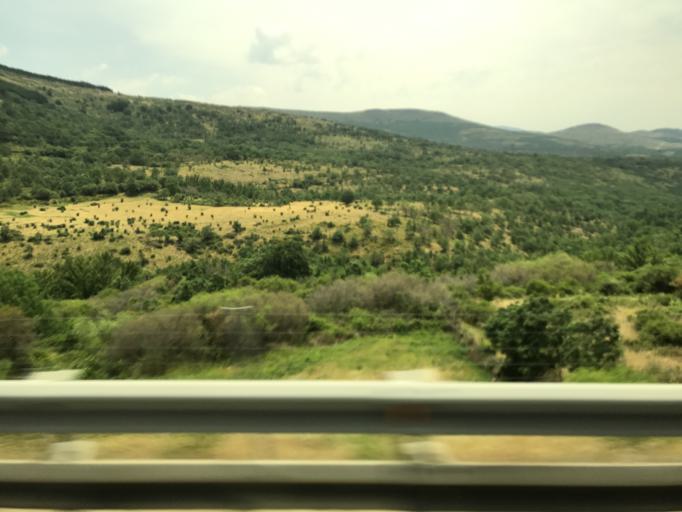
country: ES
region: Madrid
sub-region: Provincia de Madrid
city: Robregordo
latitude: 41.1057
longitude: -3.5916
